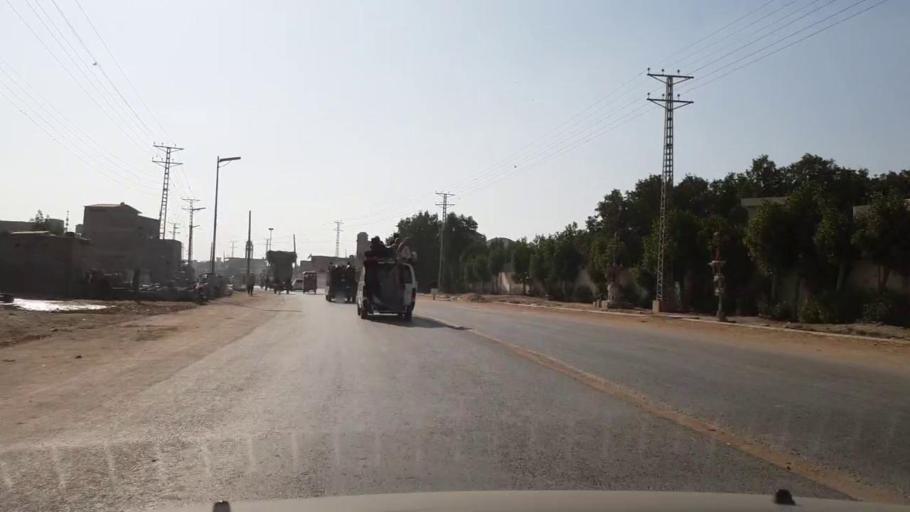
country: PK
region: Sindh
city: Tando Muhammad Khan
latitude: 25.1196
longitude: 68.5382
